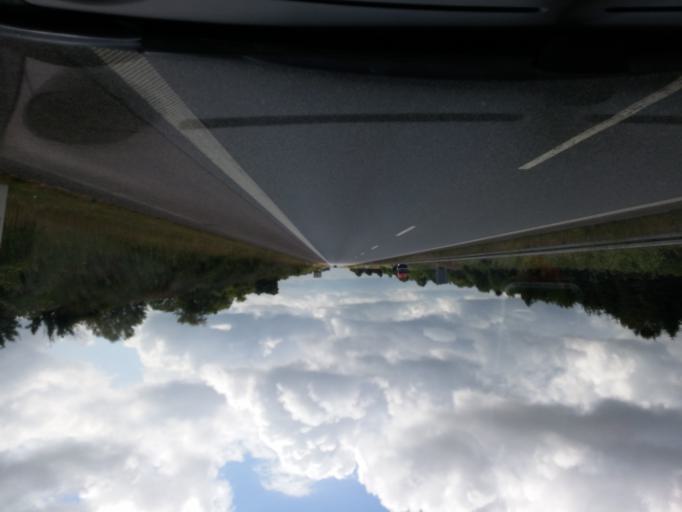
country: DK
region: South Denmark
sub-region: Faaborg-Midtfyn Kommune
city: Ringe
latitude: 55.2119
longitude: 10.5056
